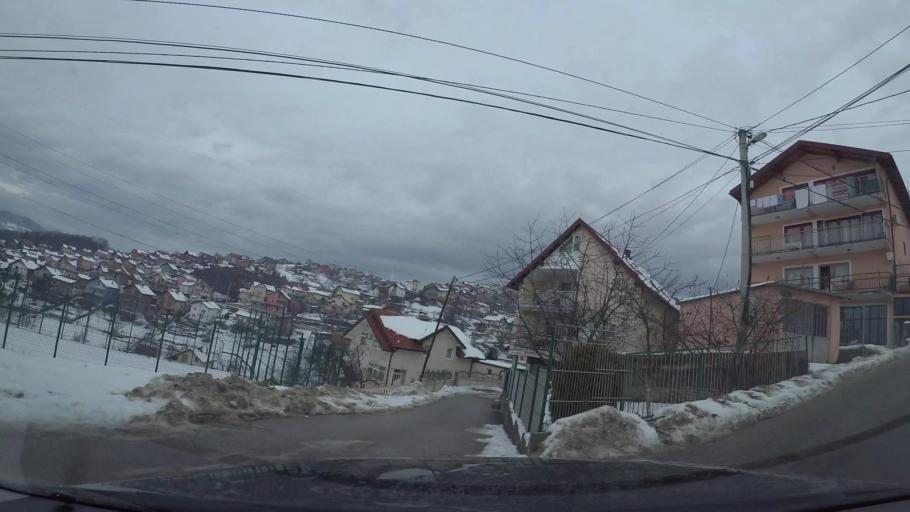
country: BA
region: Federation of Bosnia and Herzegovina
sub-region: Kanton Sarajevo
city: Sarajevo
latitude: 43.8584
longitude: 18.3317
